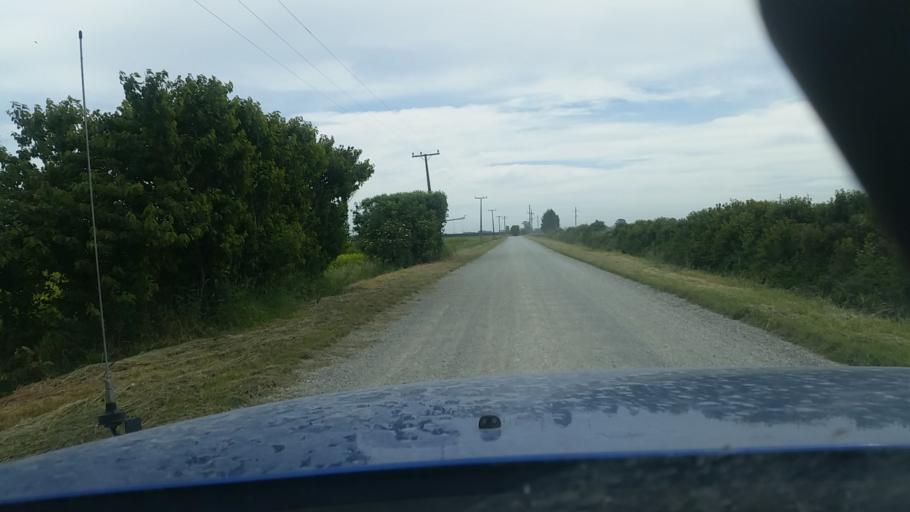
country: NZ
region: Canterbury
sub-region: Ashburton District
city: Tinwald
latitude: -44.0064
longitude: 171.7749
